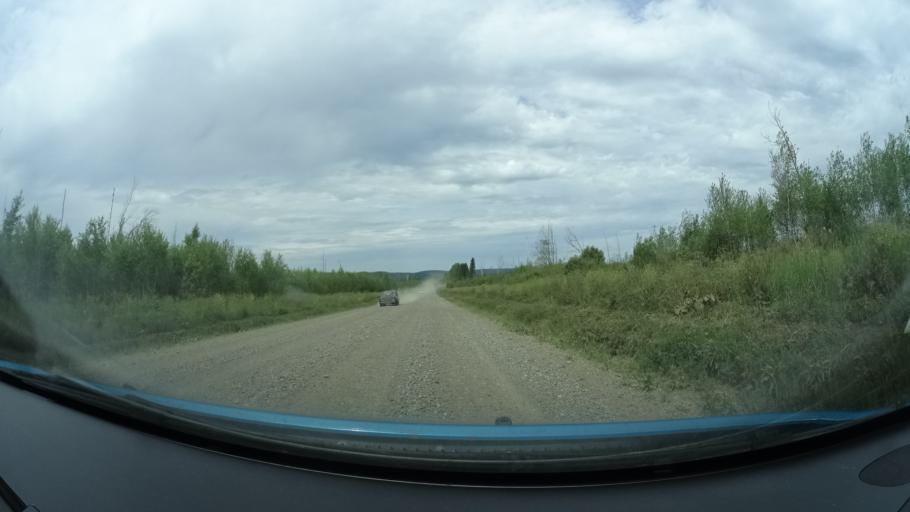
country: RU
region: Perm
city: Barda
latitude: 56.7910
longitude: 55.6751
